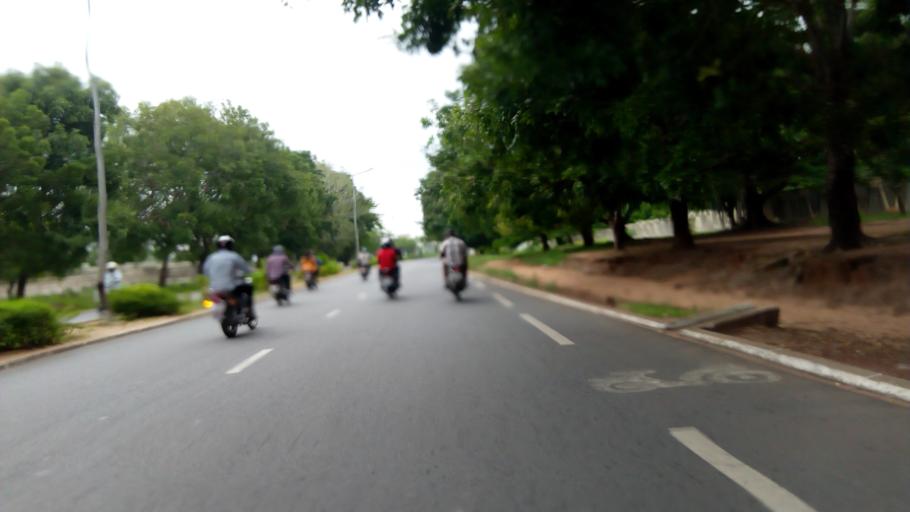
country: TG
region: Maritime
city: Lome
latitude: 6.1705
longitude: 1.2203
